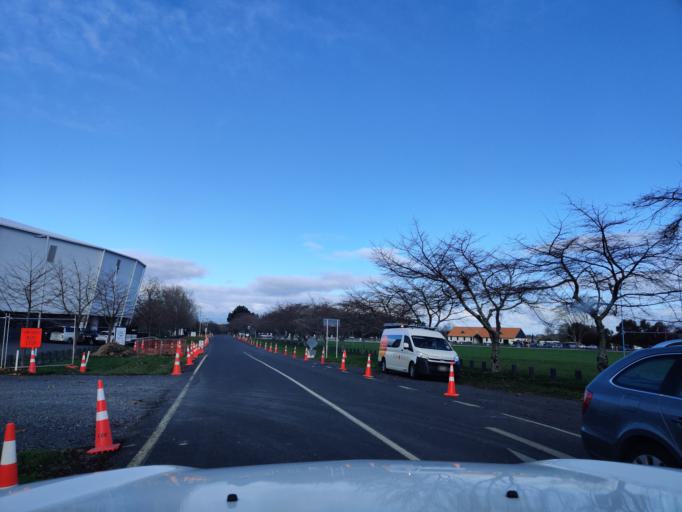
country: NZ
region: Waikato
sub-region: Waipa District
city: Cambridge
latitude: -37.8896
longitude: 175.4336
